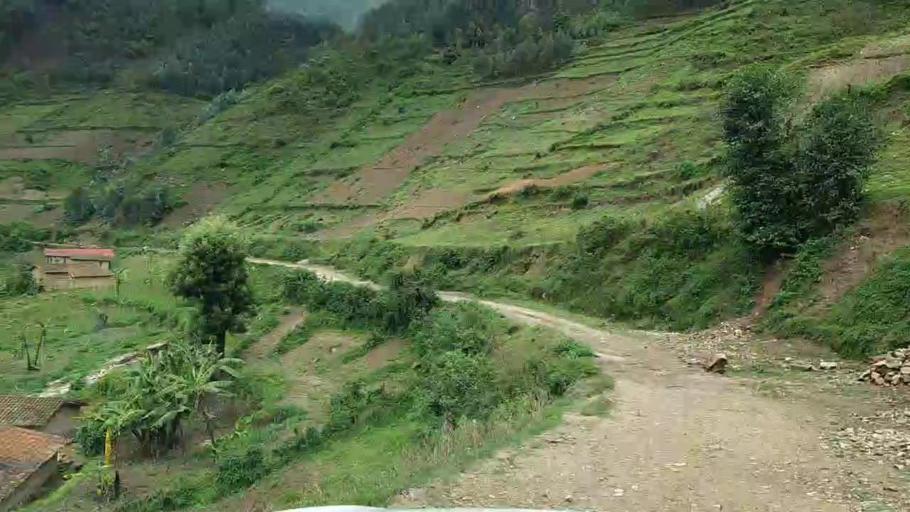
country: RW
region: Southern Province
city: Gikongoro
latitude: -2.3607
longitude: 29.4971
